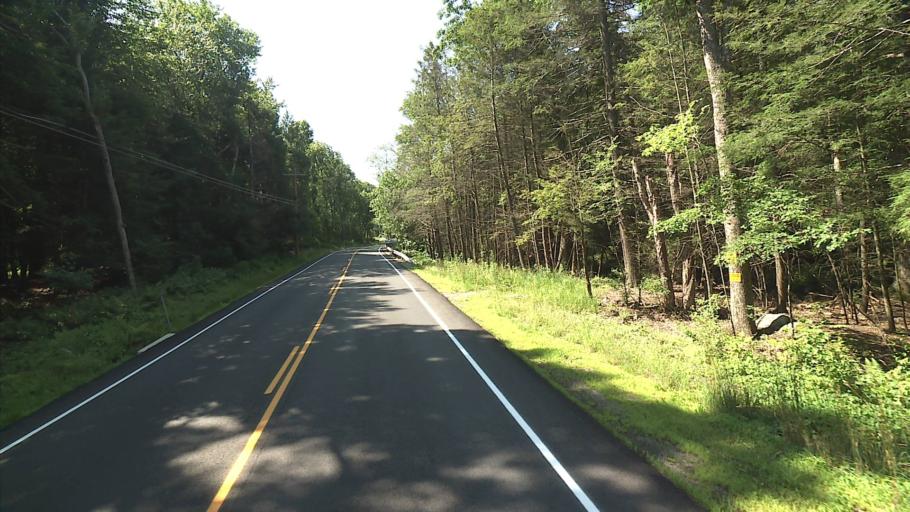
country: US
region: Connecticut
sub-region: Litchfield County
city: Terryville
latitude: 41.7198
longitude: -73.0134
